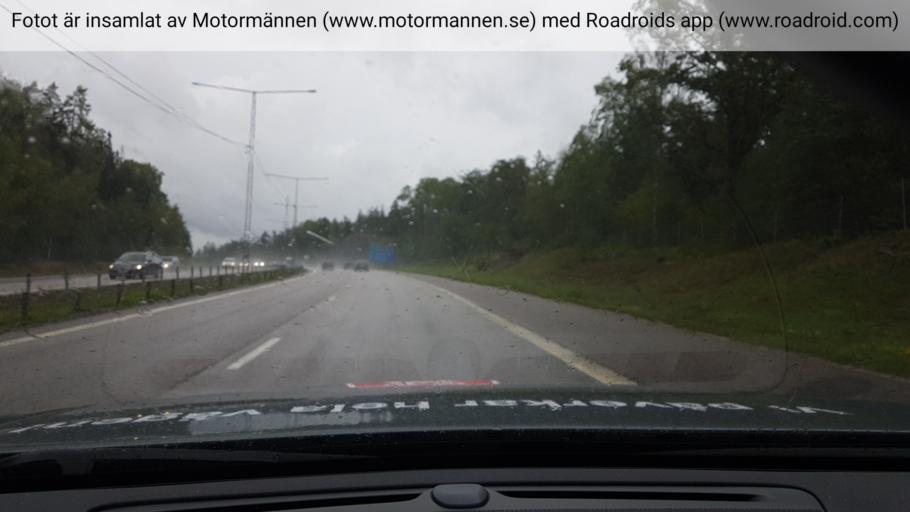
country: SE
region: Stockholm
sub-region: Haninge Kommun
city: Haninge
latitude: 59.1372
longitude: 18.1591
